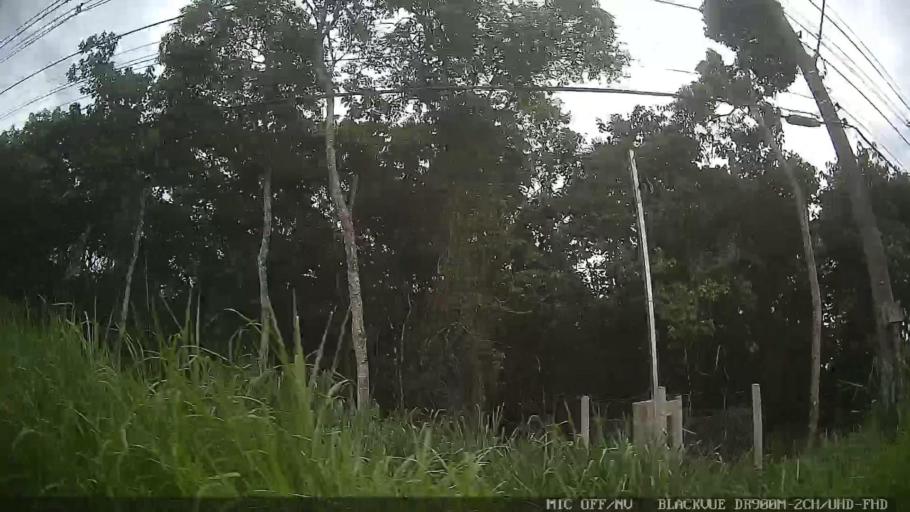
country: BR
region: Sao Paulo
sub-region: Aruja
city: Aruja
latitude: -23.4264
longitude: -46.2313
